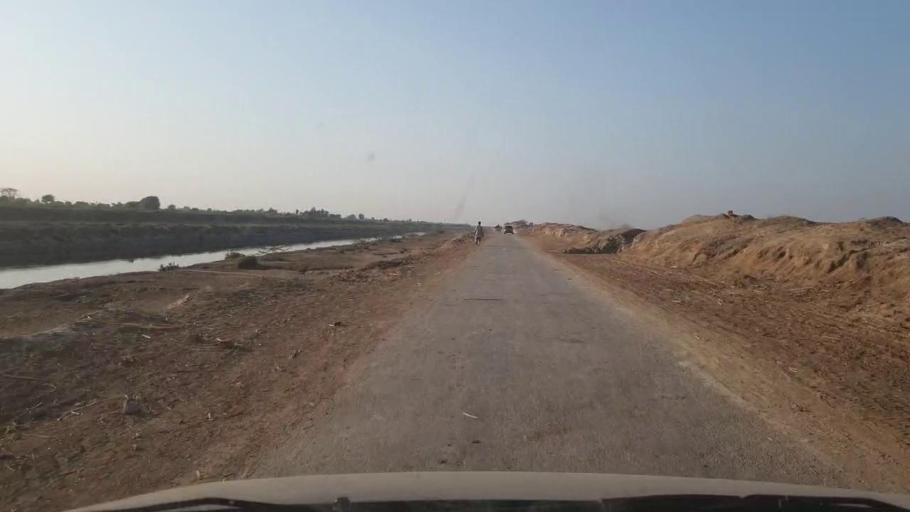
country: PK
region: Sindh
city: Samaro
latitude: 25.2830
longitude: 69.3389
